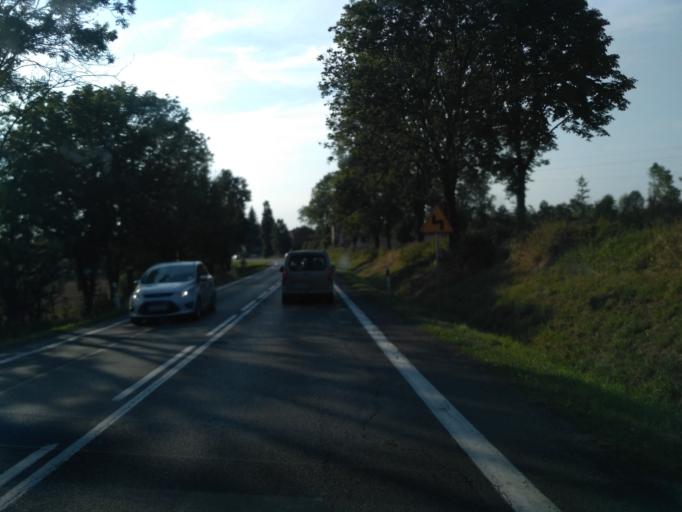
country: PL
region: Subcarpathian Voivodeship
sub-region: Powiat brzozowski
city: Humniska
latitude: 49.6684
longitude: 22.0651
